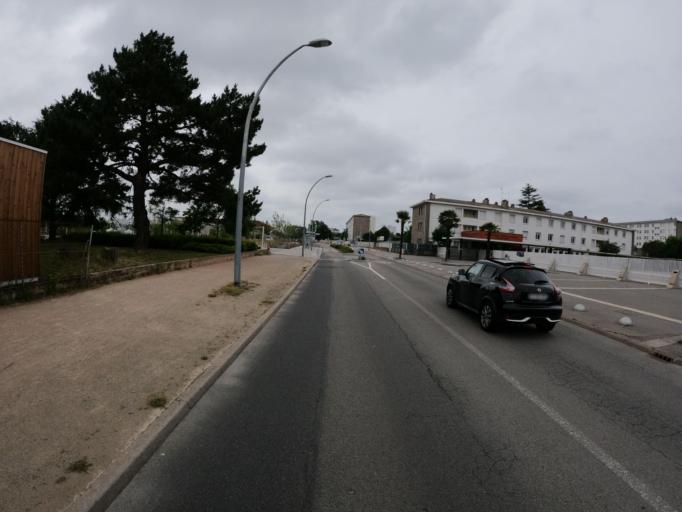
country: FR
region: Pays de la Loire
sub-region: Departement de la Loire-Atlantique
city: Saint-Nazaire
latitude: 47.2733
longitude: -2.2321
